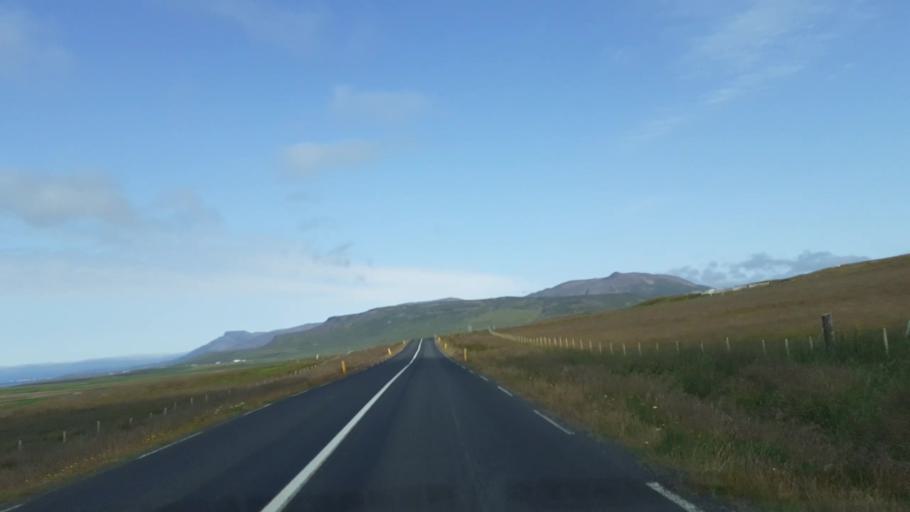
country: IS
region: Northwest
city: Saudarkrokur
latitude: 65.7015
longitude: -20.2362
